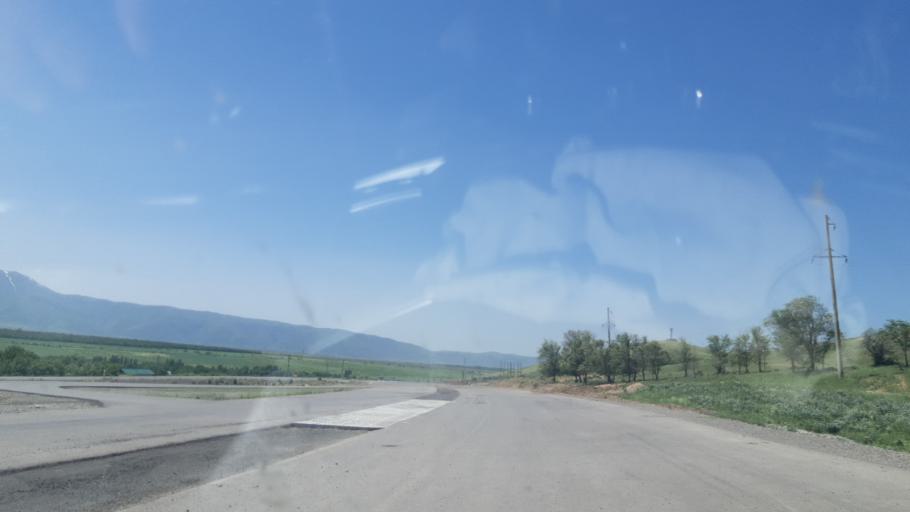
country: KZ
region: Ongtustik Qazaqstan
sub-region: Tulkibas Audany
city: Zhabagly
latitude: 42.5168
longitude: 70.5340
